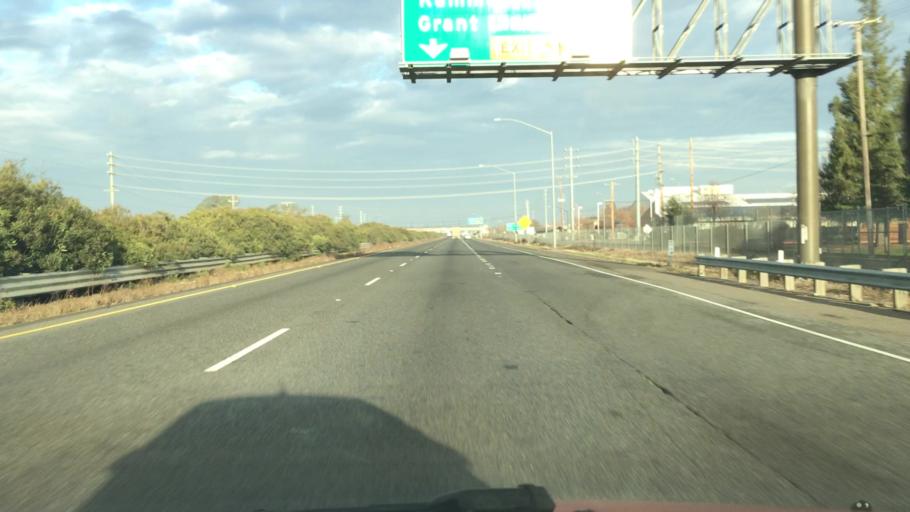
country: US
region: California
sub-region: Sacramento County
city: Elk Grove
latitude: 38.3699
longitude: -121.3554
